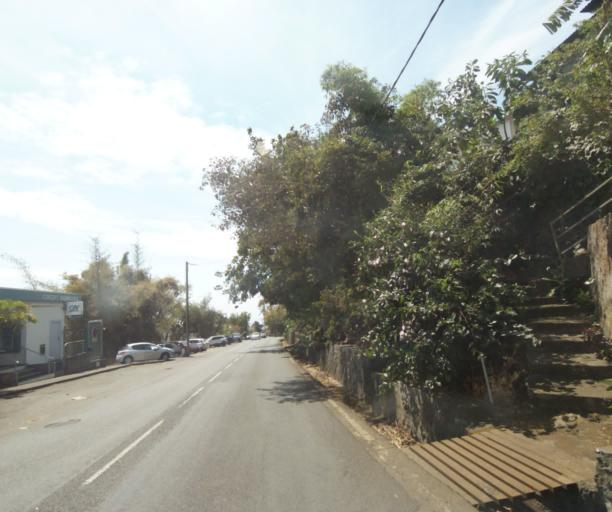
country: RE
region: Reunion
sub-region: Reunion
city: Trois-Bassins
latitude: -21.0792
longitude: 55.2694
